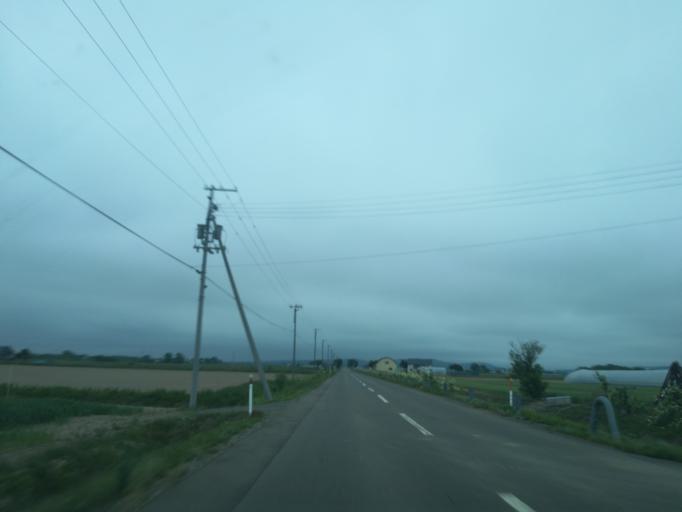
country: JP
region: Hokkaido
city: Iwamizawa
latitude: 43.1382
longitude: 141.7149
